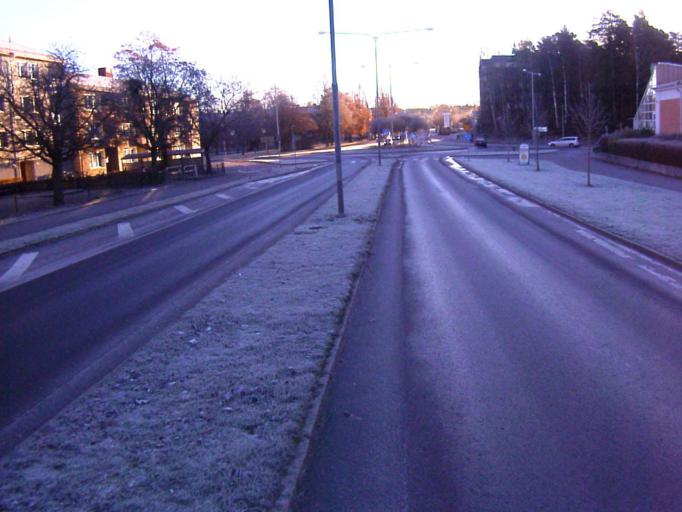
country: SE
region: Soedermanland
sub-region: Eskilstuna Kommun
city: Eskilstuna
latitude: 59.3597
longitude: 16.5181
